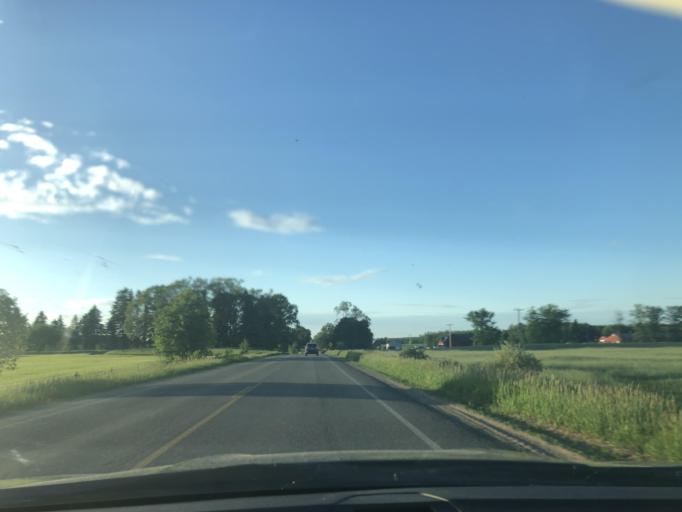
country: US
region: Michigan
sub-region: Missaukee County
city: Lake City
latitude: 44.4184
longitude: -85.0754
